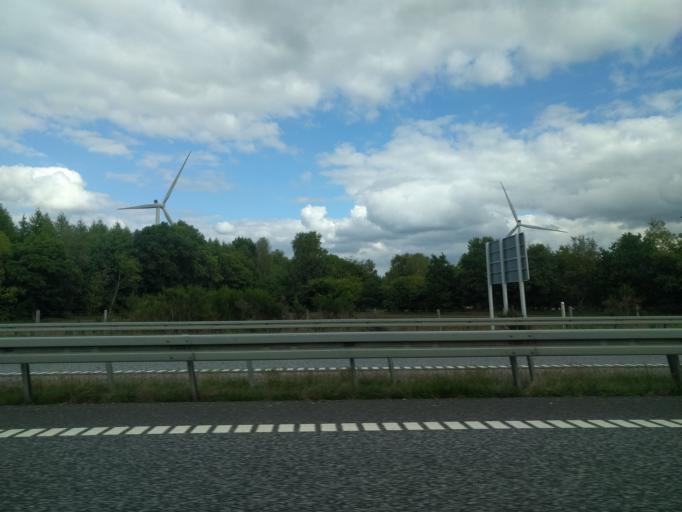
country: DK
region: Central Jutland
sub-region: Ikast-Brande Kommune
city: Brande
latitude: 55.9197
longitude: 9.1698
